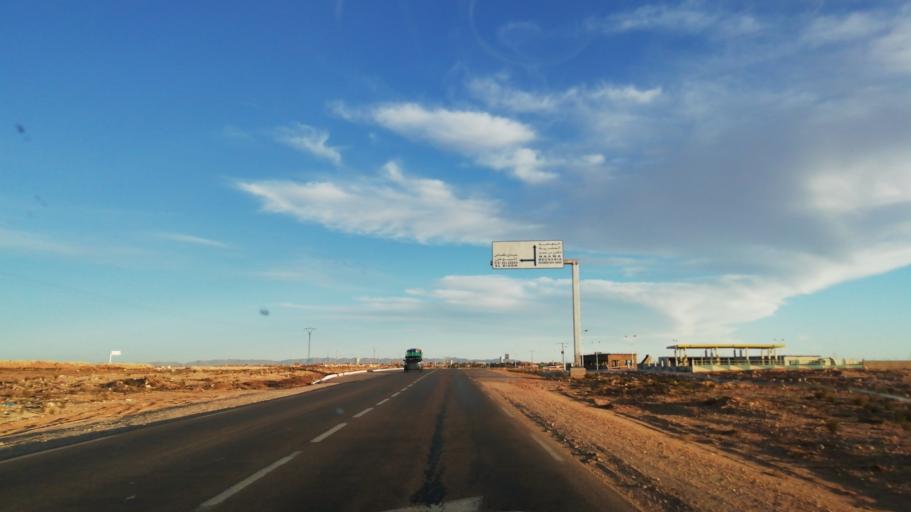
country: DZ
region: Wilaya de Naama
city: Naama
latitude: 33.7269
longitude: -0.7454
